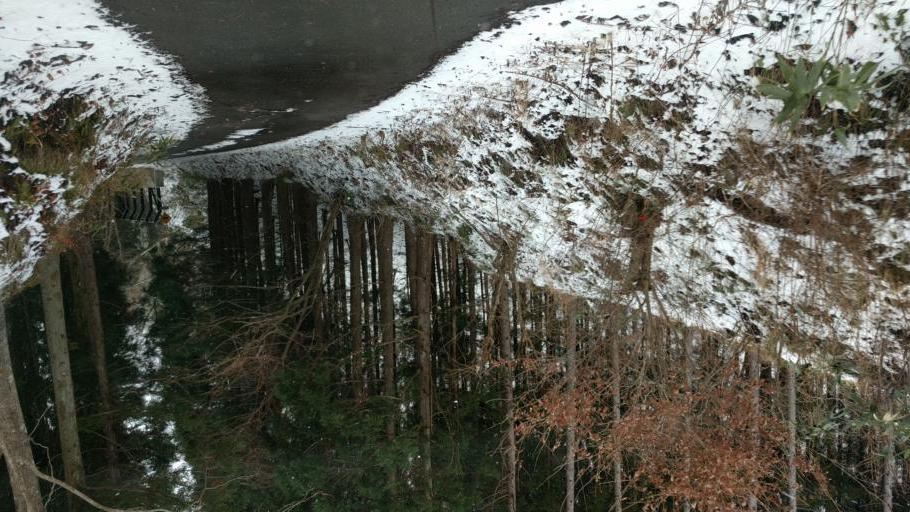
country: JP
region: Fukushima
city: Inawashiro
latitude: 37.4004
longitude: 140.0109
